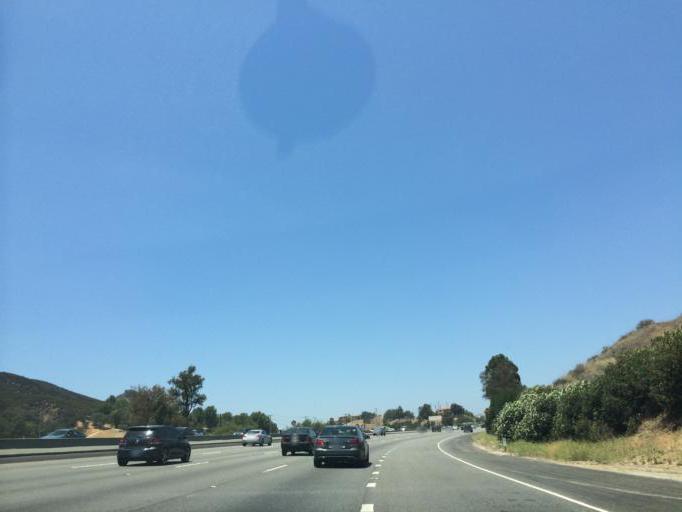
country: US
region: California
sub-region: Los Angeles County
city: Agoura
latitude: 34.1383
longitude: -118.7287
